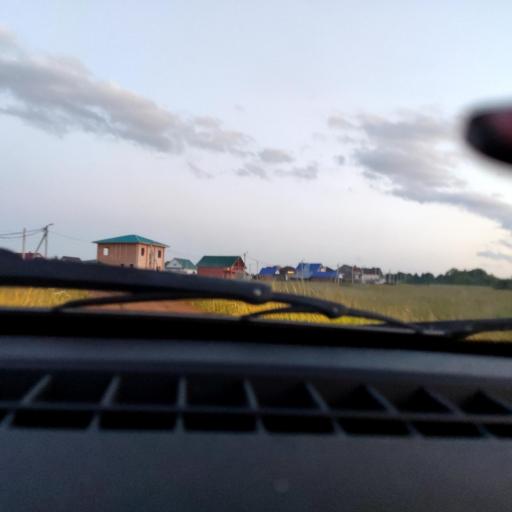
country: RU
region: Bashkortostan
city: Kabakovo
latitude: 54.6098
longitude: 56.1002
